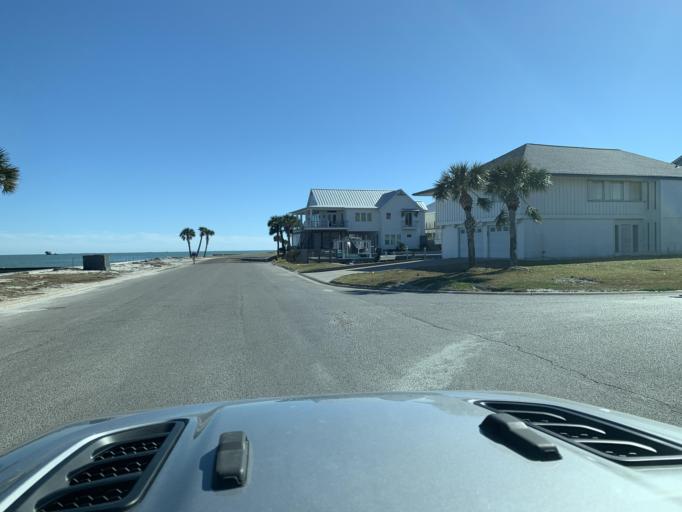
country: US
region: Texas
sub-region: Aransas County
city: Fulton
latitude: 28.0368
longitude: -97.0256
